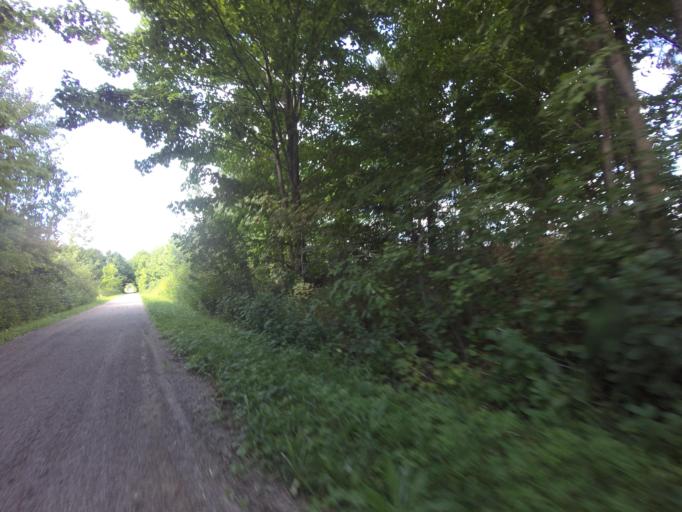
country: CA
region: Ontario
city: Huron East
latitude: 43.6678
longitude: -81.2693
